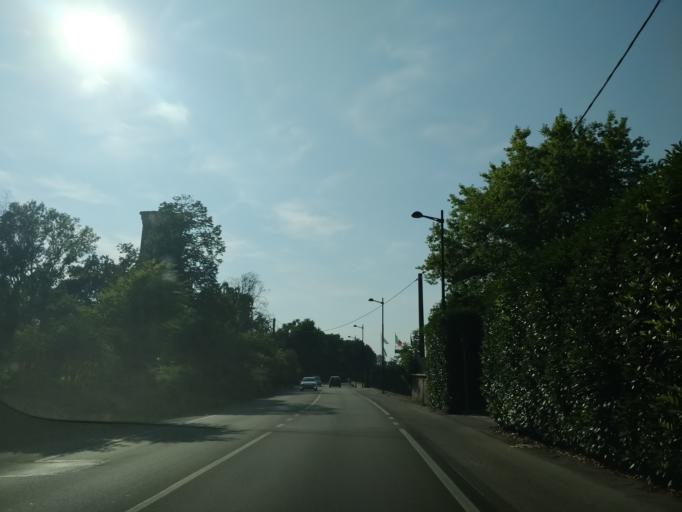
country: IT
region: Emilia-Romagna
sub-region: Provincia di Bologna
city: Progresso
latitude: 44.5595
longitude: 11.3536
